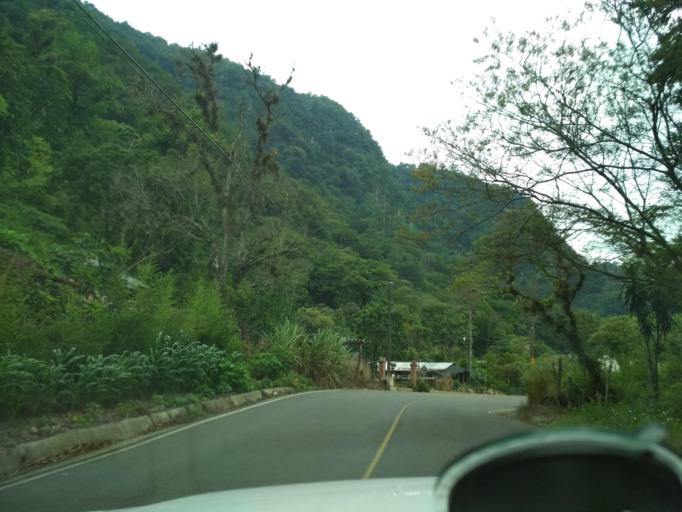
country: MX
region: Veracruz
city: Jilotepec
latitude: 19.6156
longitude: -96.9303
